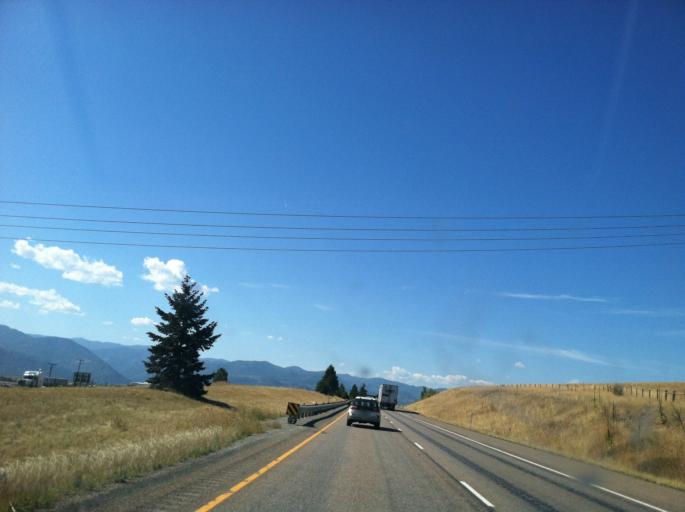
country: US
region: Montana
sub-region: Missoula County
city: Orchard Homes
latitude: 46.9385
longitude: -114.1023
